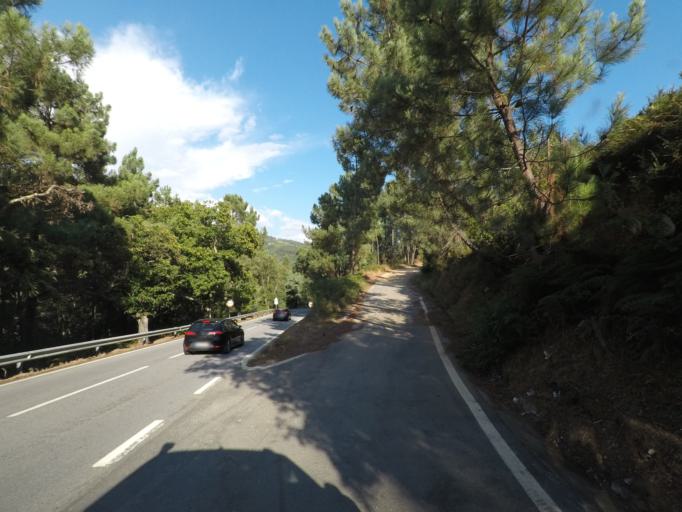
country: PT
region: Vila Real
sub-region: Mesao Frio
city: Mesao Frio
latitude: 41.1740
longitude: -7.9107
